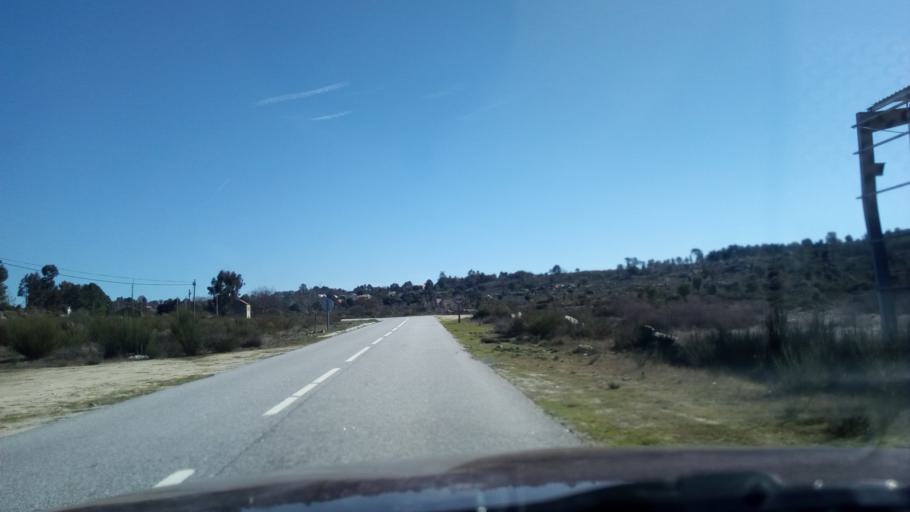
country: PT
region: Guarda
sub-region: Fornos de Algodres
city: Fornos de Algodres
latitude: 40.6041
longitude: -7.5233
